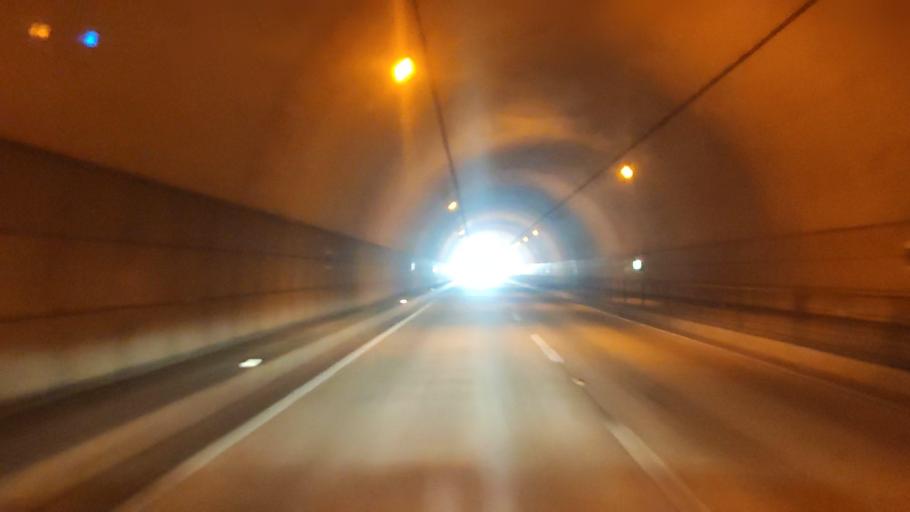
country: JP
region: Miyazaki
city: Nobeoka
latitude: 32.6861
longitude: 131.7959
